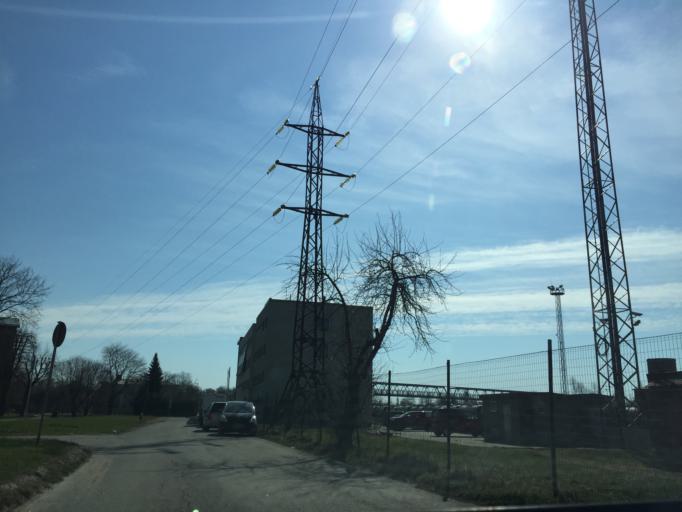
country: EE
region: Ida-Virumaa
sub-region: Narva linn
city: Narva
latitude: 59.3703
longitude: 28.1942
